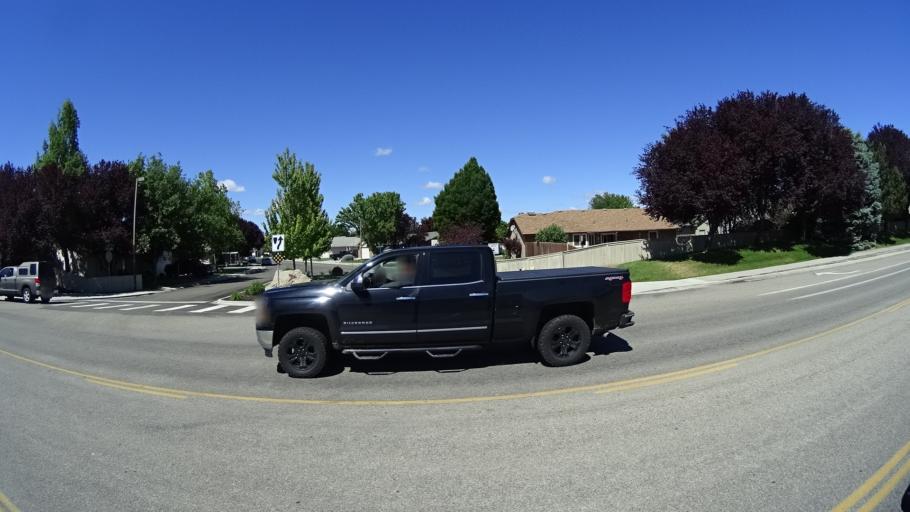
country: US
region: Idaho
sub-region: Ada County
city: Meridian
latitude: 43.6322
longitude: -116.3745
